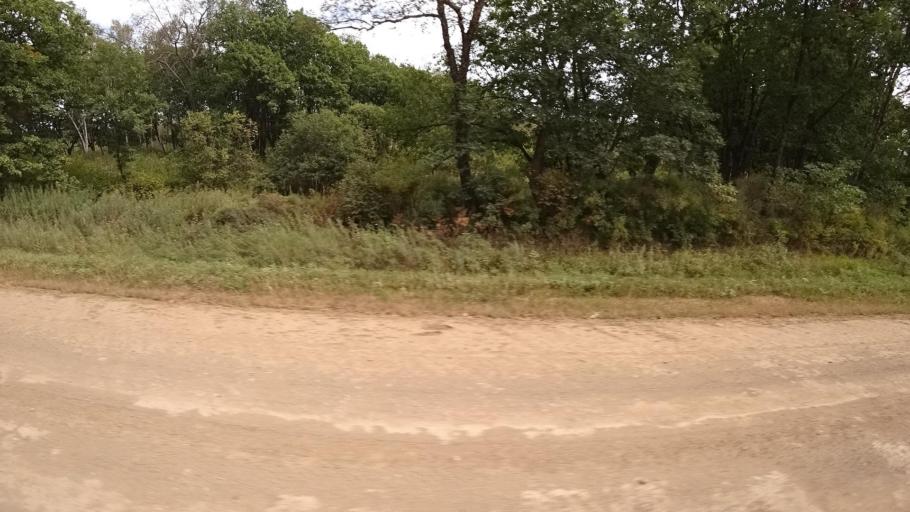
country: RU
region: Primorskiy
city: Yakovlevka
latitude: 44.4887
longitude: 133.5845
